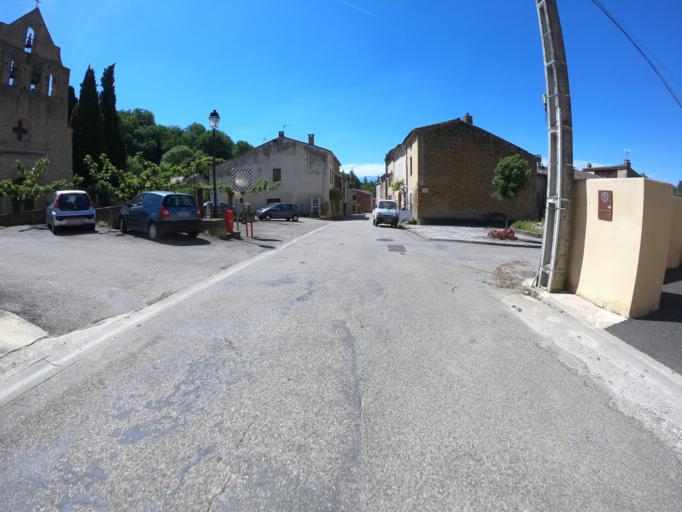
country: FR
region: Midi-Pyrenees
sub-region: Departement de l'Ariege
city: Mirepoix
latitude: 43.0927
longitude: 1.7787
